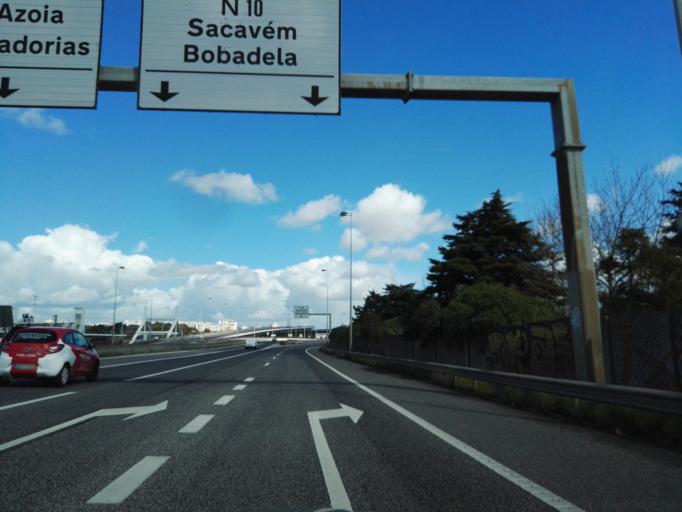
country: PT
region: Lisbon
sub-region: Loures
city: Sacavem
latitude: 38.7927
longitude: -9.0998
